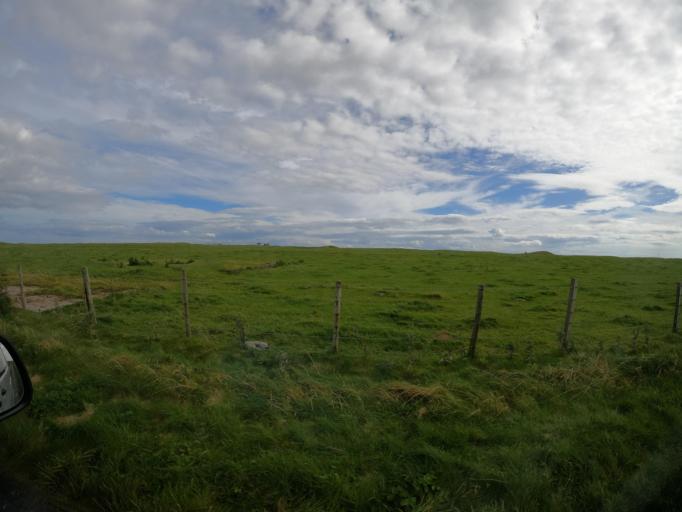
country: GB
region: Scotland
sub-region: Eilean Siar
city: Barra
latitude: 56.4808
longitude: -6.9003
